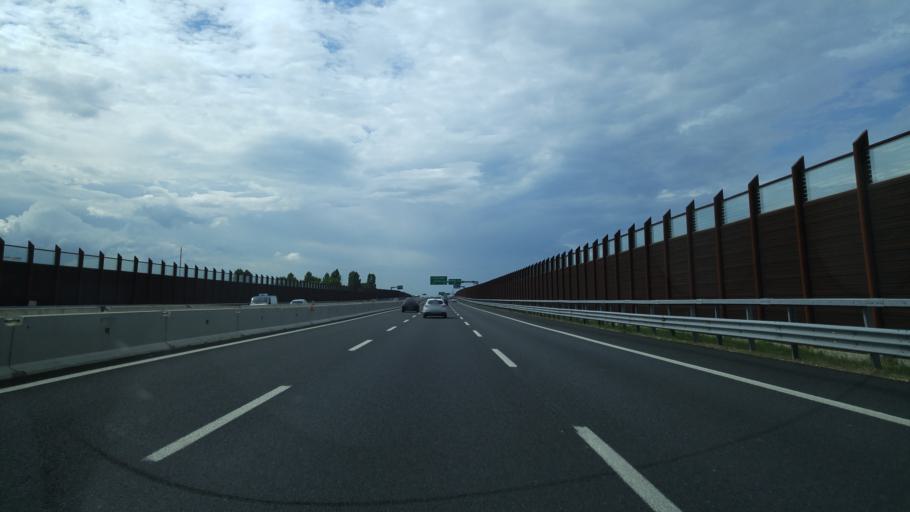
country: IT
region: Emilia-Romagna
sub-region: Provincia di Rimini
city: Rimini
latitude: 44.0289
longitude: 12.5775
